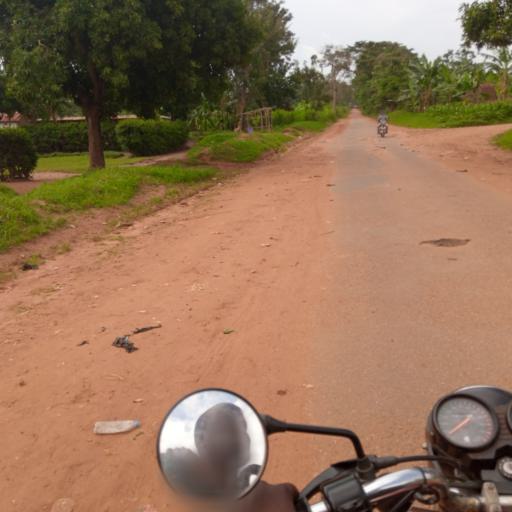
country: UG
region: Eastern Region
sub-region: Mbale District
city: Mbale
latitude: 1.0895
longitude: 34.1849
